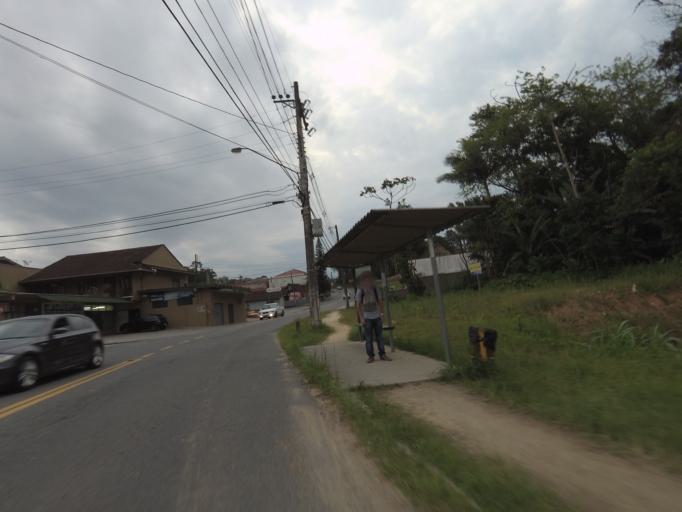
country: BR
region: Santa Catarina
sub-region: Blumenau
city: Blumenau
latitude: -26.8754
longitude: -49.0550
